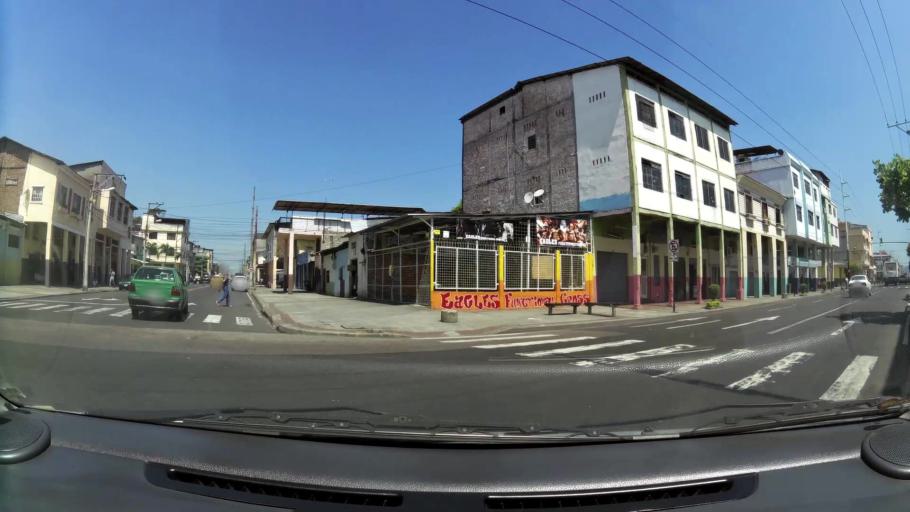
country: EC
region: Guayas
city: Guayaquil
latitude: -2.2068
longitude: -79.8977
